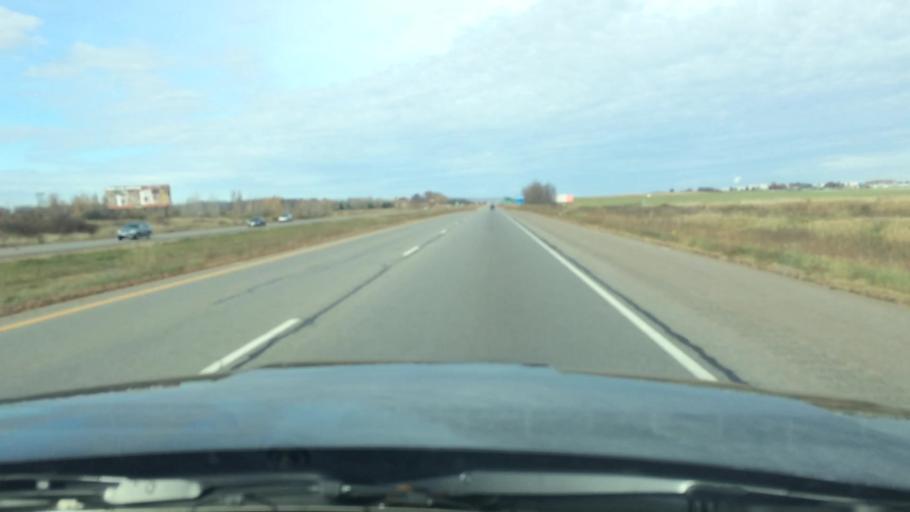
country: US
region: Wisconsin
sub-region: Marathon County
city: Mosinee
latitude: 44.7723
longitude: -89.6800
